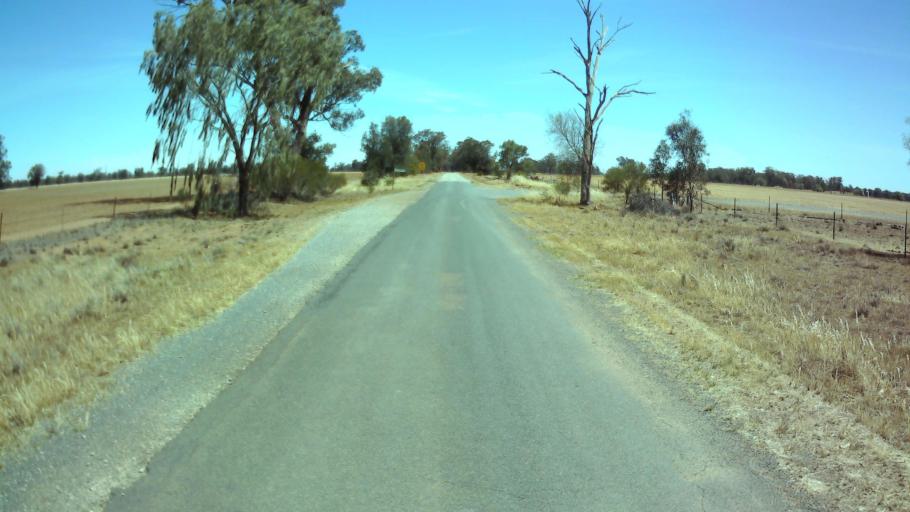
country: AU
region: New South Wales
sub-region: Weddin
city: Grenfell
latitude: -33.9059
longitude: 147.6854
